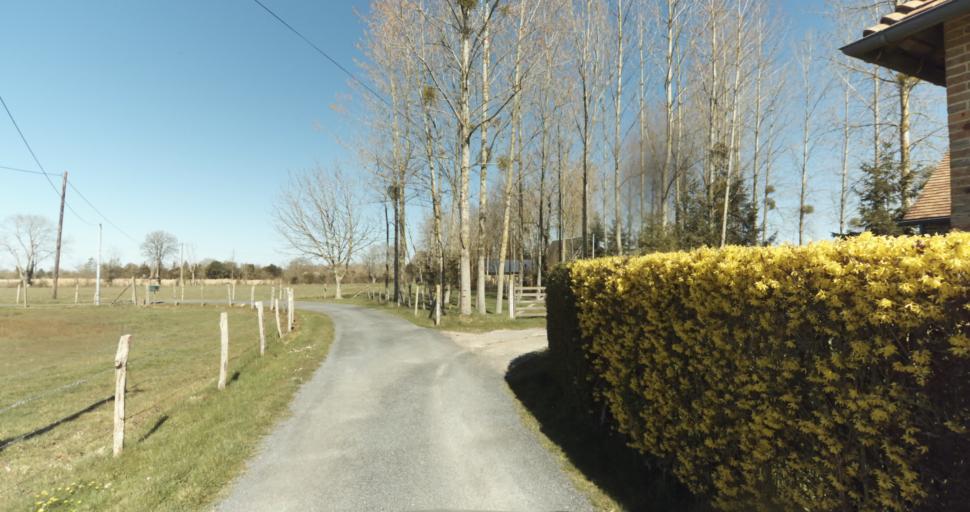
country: FR
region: Lower Normandy
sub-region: Departement du Calvados
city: Livarot
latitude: 49.0175
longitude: 0.1096
